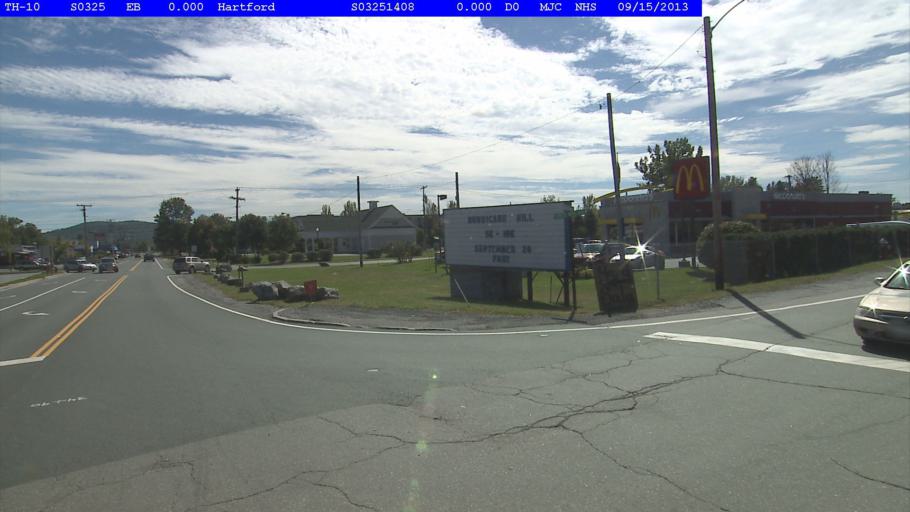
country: US
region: Vermont
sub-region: Windsor County
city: White River Junction
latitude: 43.6470
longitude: -72.3355
